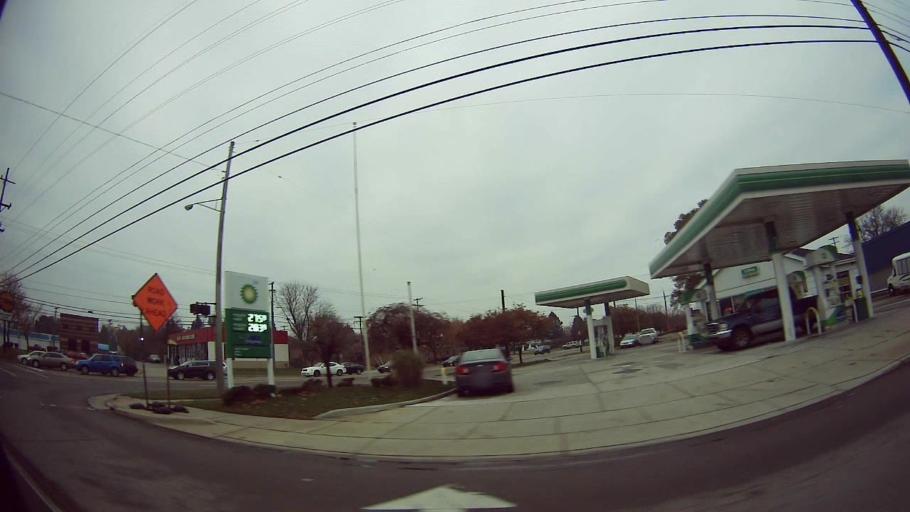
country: US
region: Michigan
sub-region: Oakland County
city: Bingham Farms
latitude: 42.4723
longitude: -83.2822
